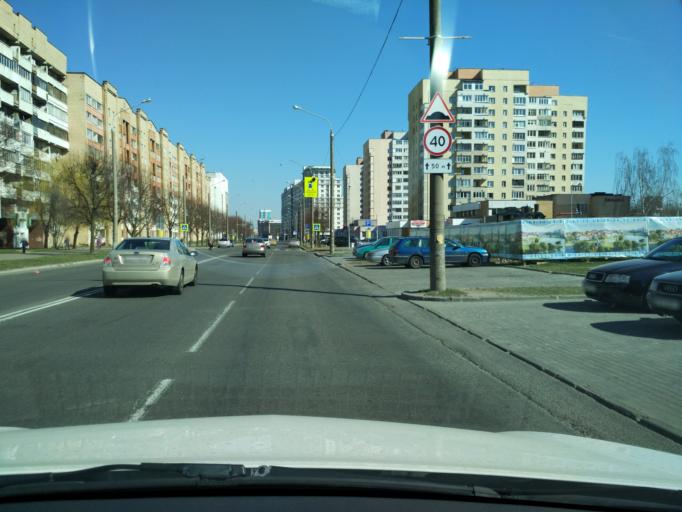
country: BY
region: Minsk
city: Minsk
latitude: 53.8785
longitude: 27.5376
